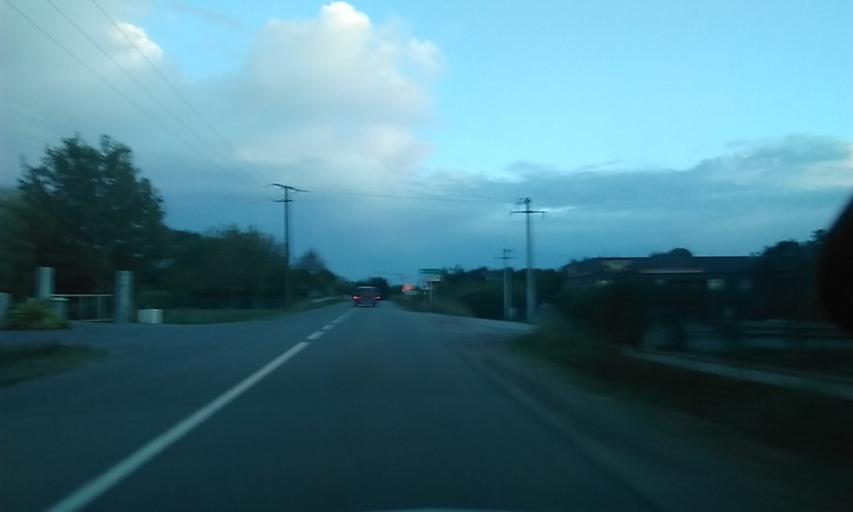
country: FR
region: Brittany
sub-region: Departement d'Ille-et-Vilaine
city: Saint-Thurial
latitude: 48.0472
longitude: -1.9299
